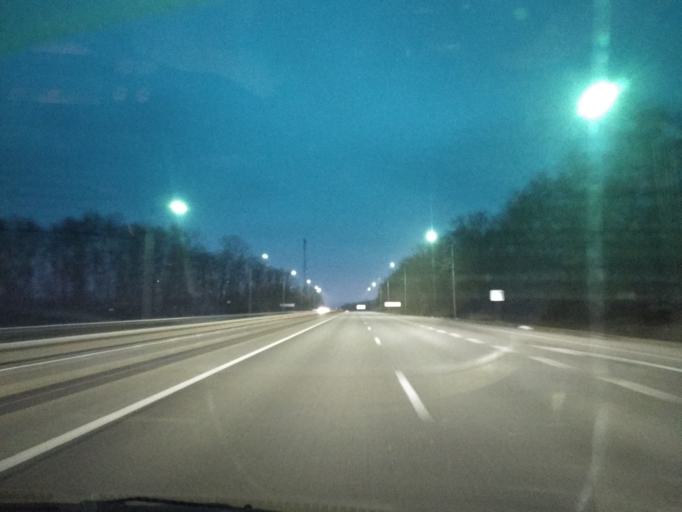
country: RU
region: Krasnodarskiy
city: Saratovskaya
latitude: 44.7102
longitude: 39.2071
